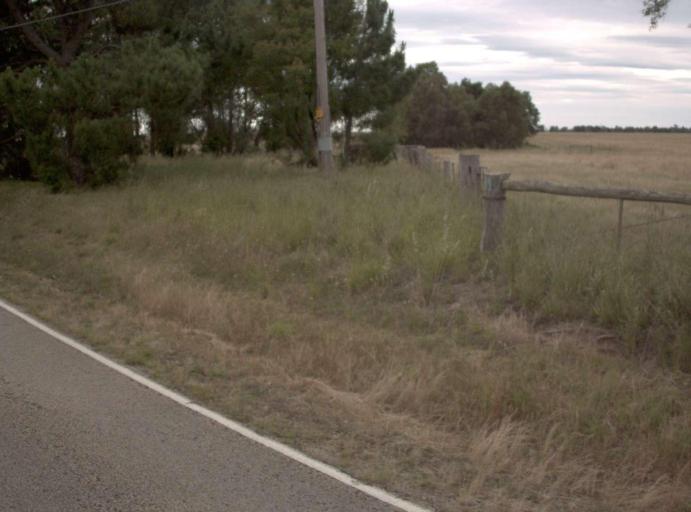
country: AU
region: Victoria
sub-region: East Gippsland
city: Bairnsdale
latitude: -37.9730
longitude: 147.4668
